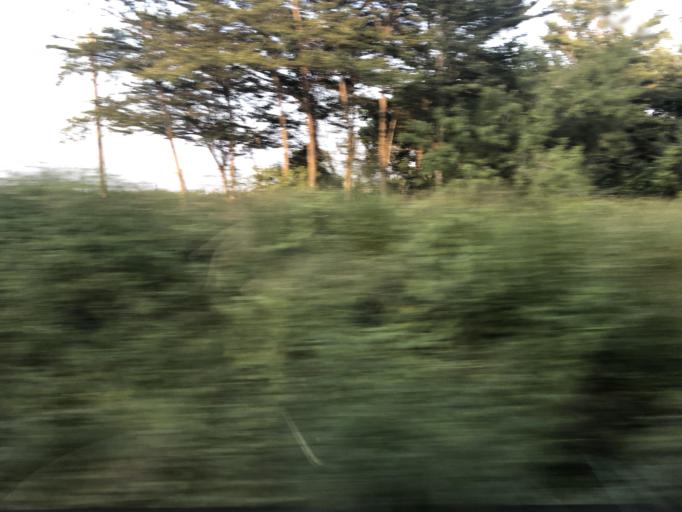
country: TW
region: Taiwan
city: Xinying
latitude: 23.1565
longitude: 120.2752
